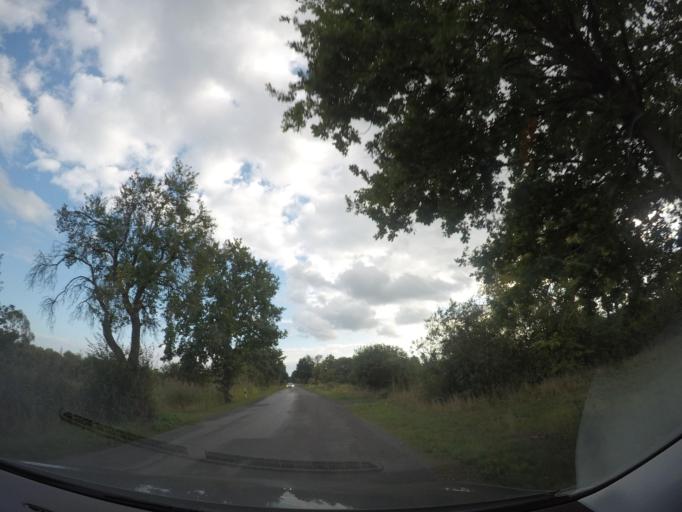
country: DE
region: Saxony-Anhalt
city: Mieste
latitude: 52.4836
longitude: 11.1362
